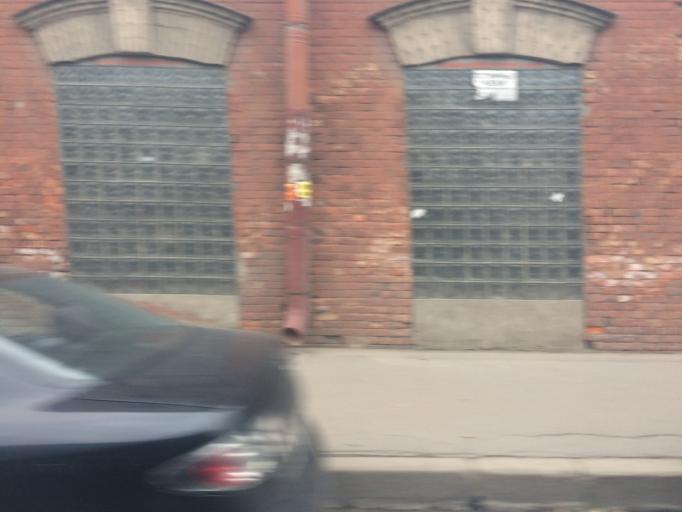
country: RU
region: St.-Petersburg
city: Obukhovo
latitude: 59.8624
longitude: 30.4767
